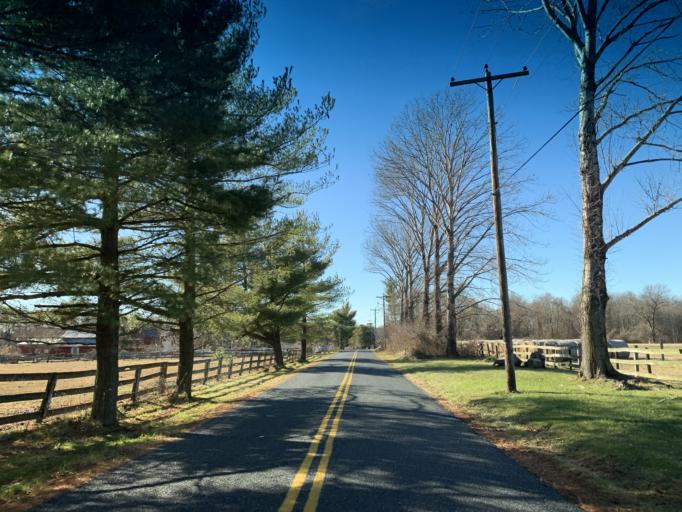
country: US
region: Maryland
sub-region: Harford County
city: Riverside
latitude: 39.5353
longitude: -76.2467
